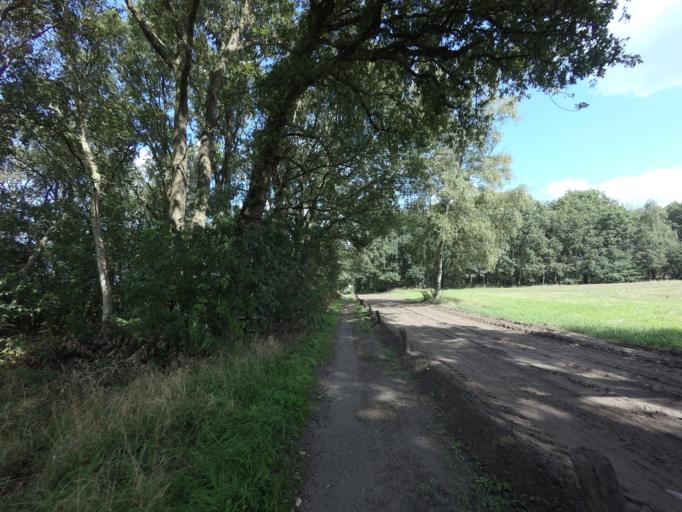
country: NL
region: Drenthe
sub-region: Gemeente Westerveld
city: Dwingeloo
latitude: 52.8839
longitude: 6.3874
